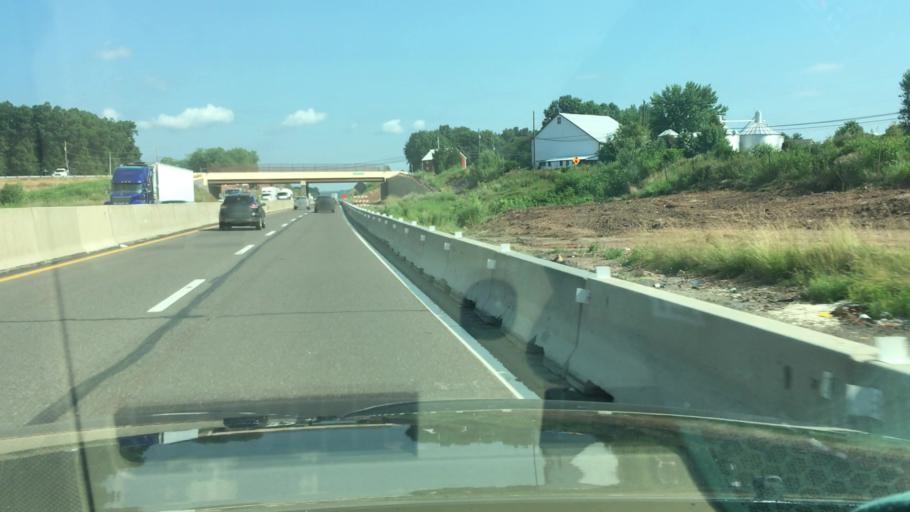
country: US
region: Pennsylvania
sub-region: Montgomery County
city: Harleysville
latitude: 40.2985
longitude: -75.3692
